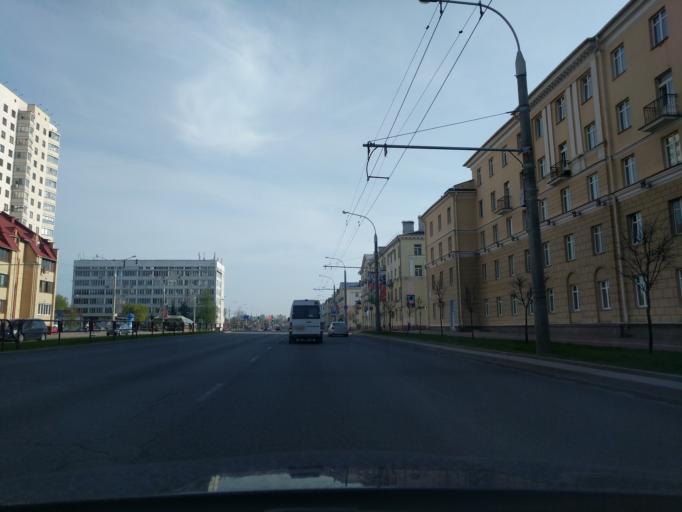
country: BY
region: Minsk
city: Minsk
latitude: 53.8652
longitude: 27.5708
